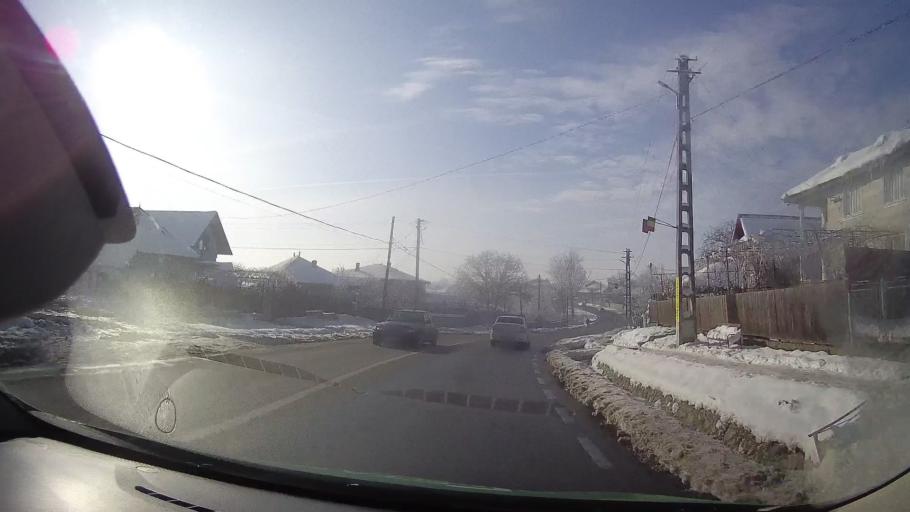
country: RO
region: Iasi
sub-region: Comuna Motca
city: Motca
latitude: 47.2398
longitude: 26.6061
